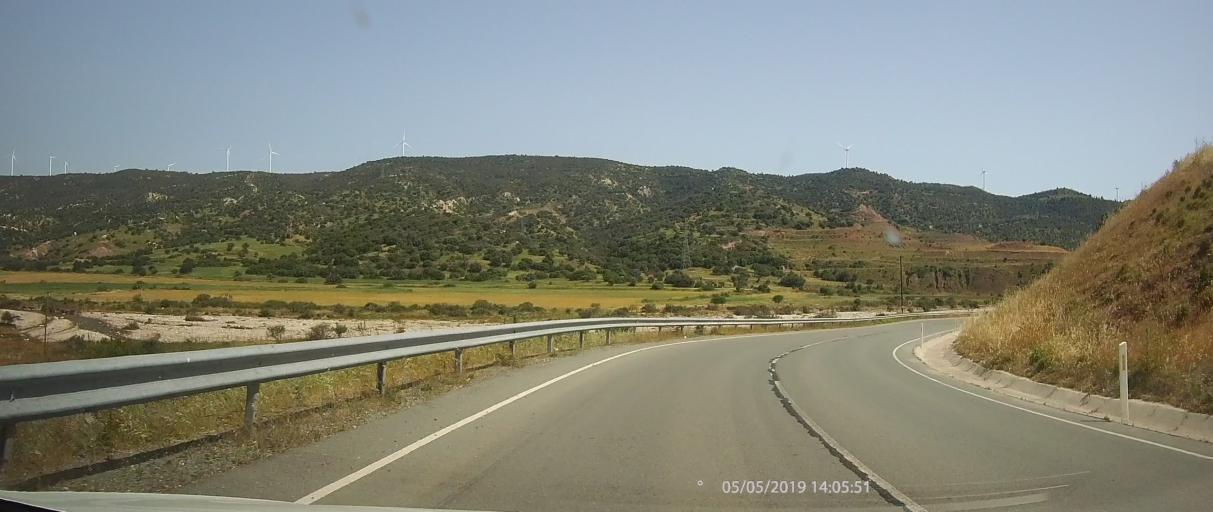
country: CY
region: Limassol
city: Pissouri
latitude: 34.7488
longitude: 32.6093
